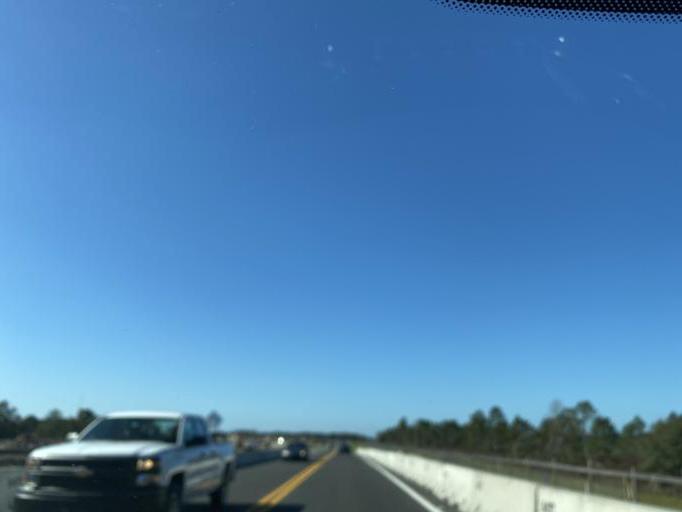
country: US
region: Florida
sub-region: Lake County
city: Mount Plymouth
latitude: 28.8144
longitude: -81.5000
